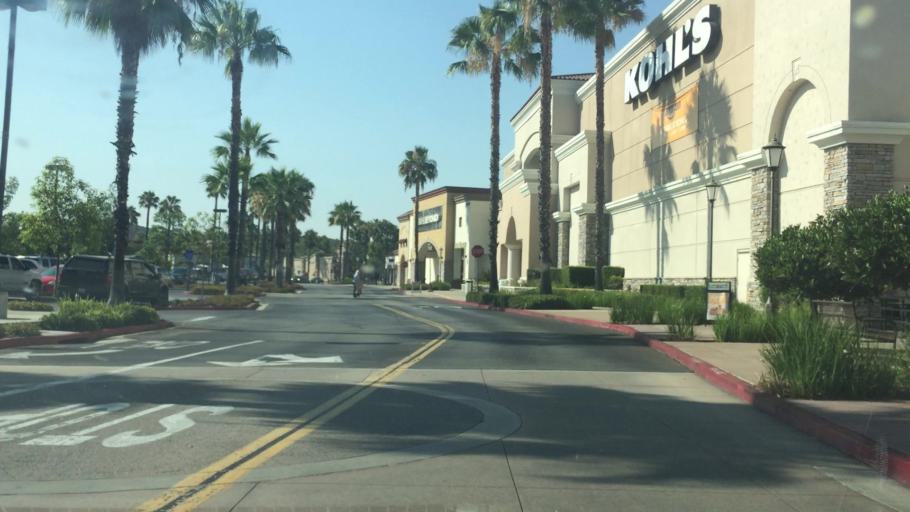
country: US
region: California
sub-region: Orange County
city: Rancho Santa Margarita
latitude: 33.6406
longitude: -117.5945
